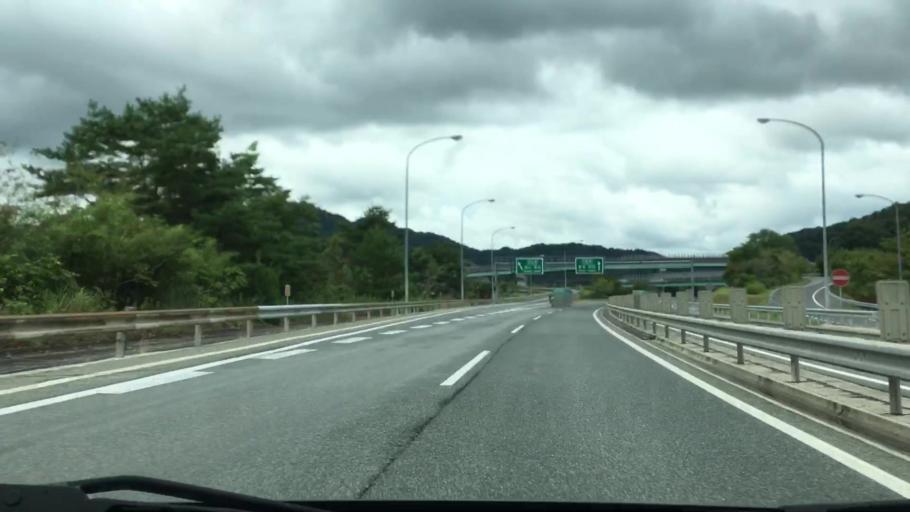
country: JP
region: Okayama
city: Takahashi
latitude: 34.9863
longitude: 133.6863
